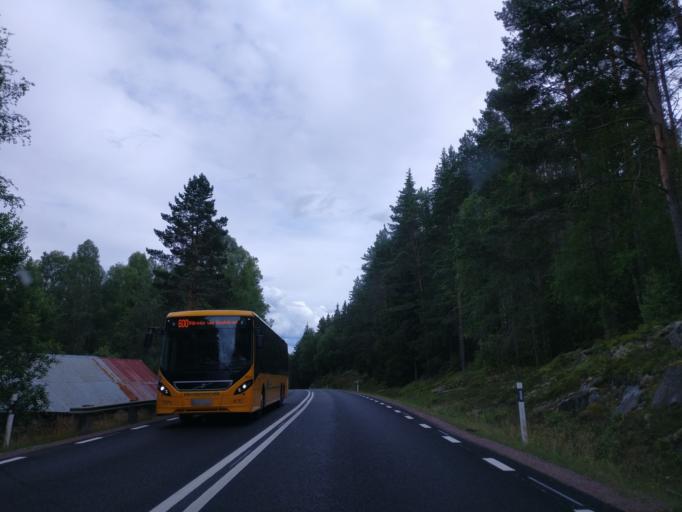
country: SE
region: Vaermland
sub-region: Hagfors Kommun
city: Hagfors
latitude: 60.0561
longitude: 13.5553
